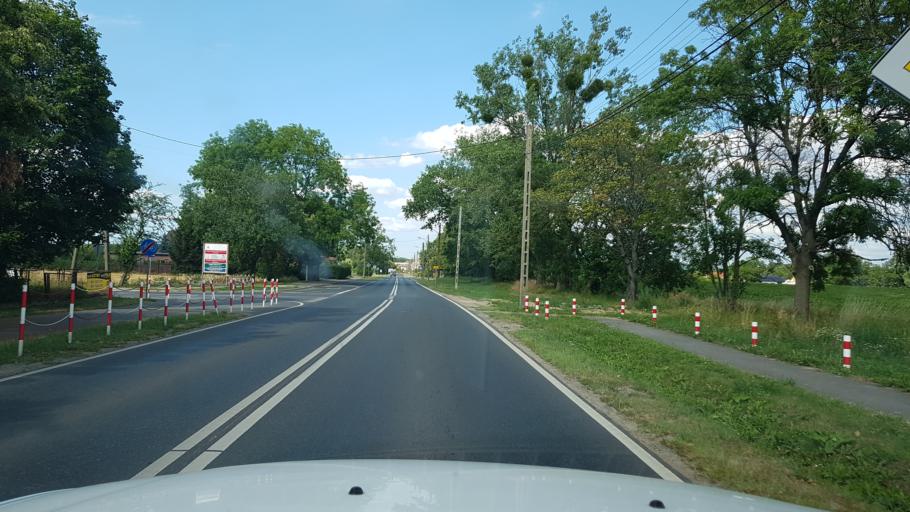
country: PL
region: West Pomeranian Voivodeship
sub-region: Powiat pyrzycki
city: Pyrzyce
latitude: 53.1285
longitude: 14.8888
